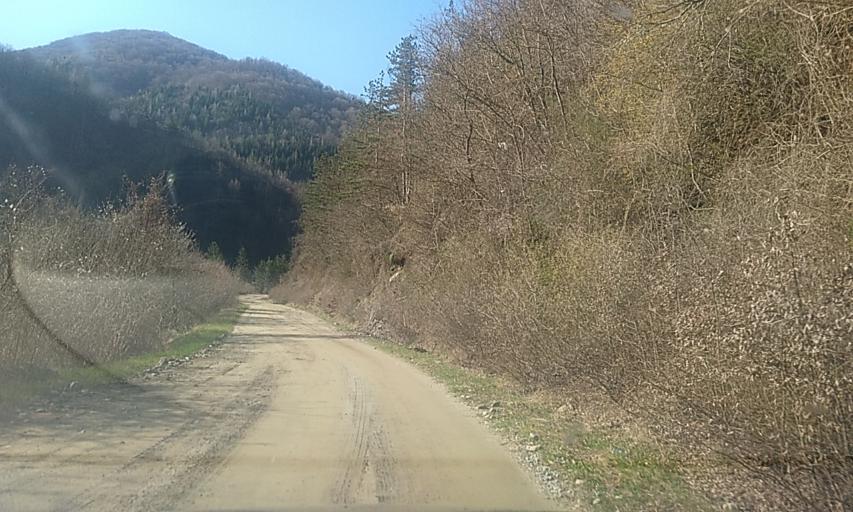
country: RS
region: Central Serbia
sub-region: Pcinjski Okrug
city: Bosilegrad
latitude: 42.3874
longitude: 22.4482
